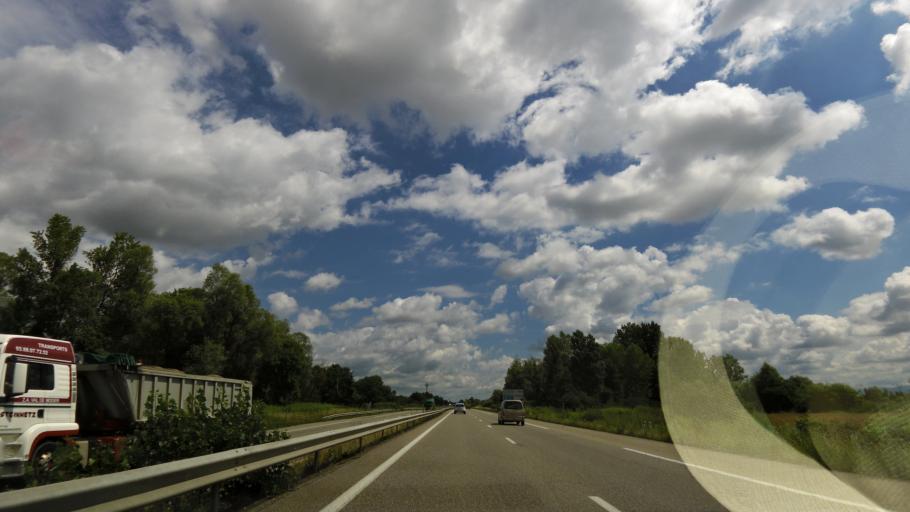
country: FR
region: Alsace
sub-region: Departement du Bas-Rhin
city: Gambsheim
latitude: 48.7125
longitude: 7.8663
